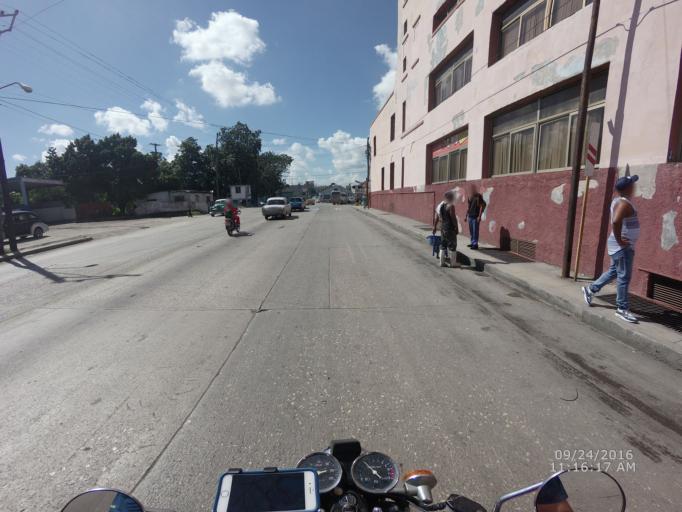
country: CU
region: La Habana
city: La Habana Vieja
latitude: 23.1146
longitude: -82.3596
